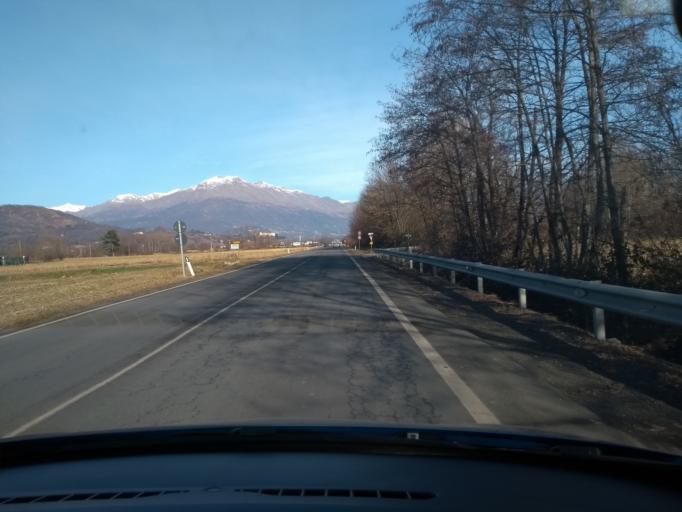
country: IT
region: Piedmont
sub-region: Provincia di Torino
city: Busano
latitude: 45.3404
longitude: 7.6554
